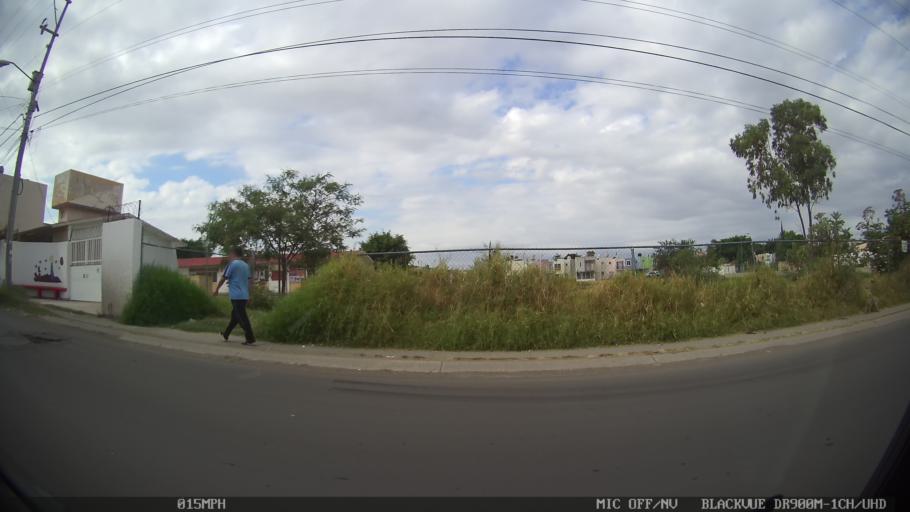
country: MX
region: Jalisco
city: Tonala
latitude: 20.6625
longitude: -103.2381
